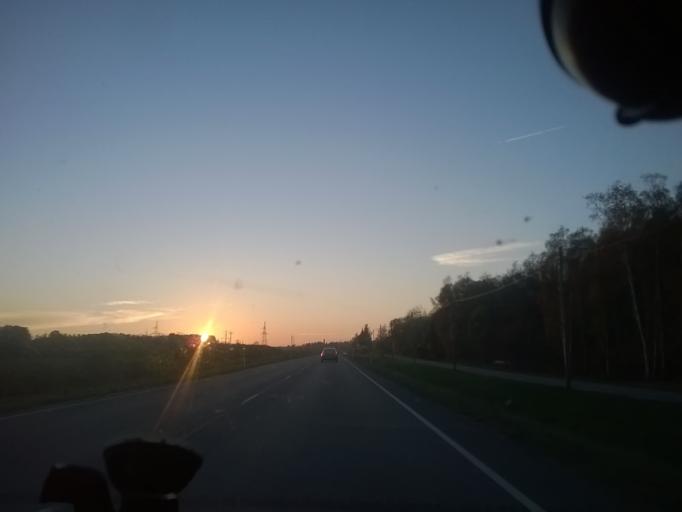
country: EE
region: Laeaene
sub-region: Ridala Parish
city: Uuemoisa
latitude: 58.9558
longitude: 23.7653
